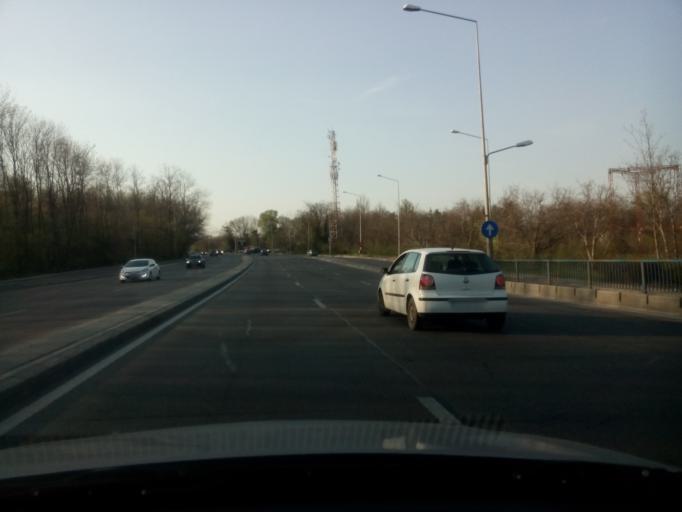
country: RO
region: Ilfov
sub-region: Comuna Otopeni
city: Otopeni
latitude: 44.5157
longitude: 26.0797
